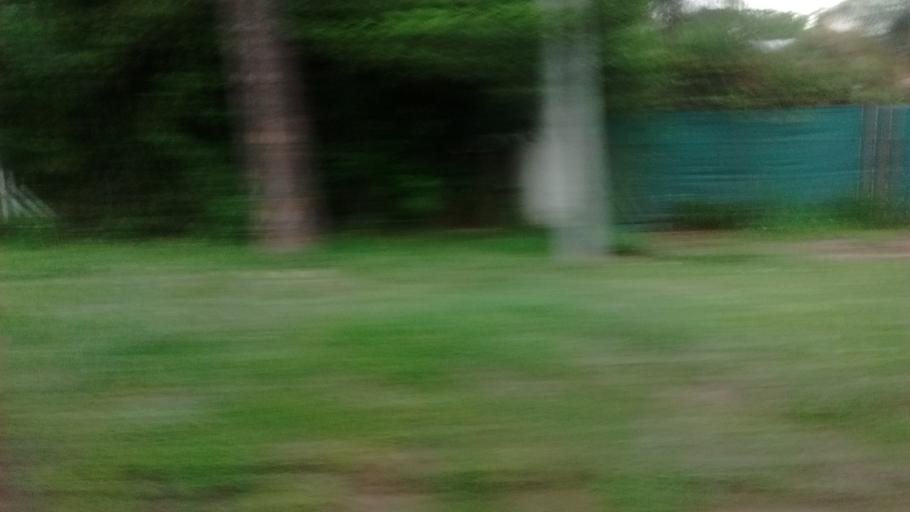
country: AR
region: Santa Fe
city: Funes
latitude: -32.9296
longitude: -60.8229
